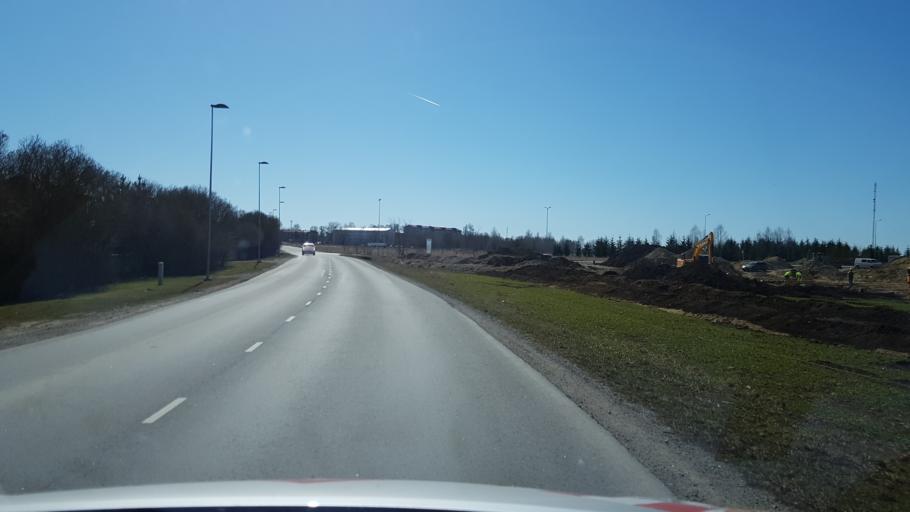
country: EE
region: Laeaene-Virumaa
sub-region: Rakvere linn
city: Rakvere
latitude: 59.3654
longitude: 26.3703
